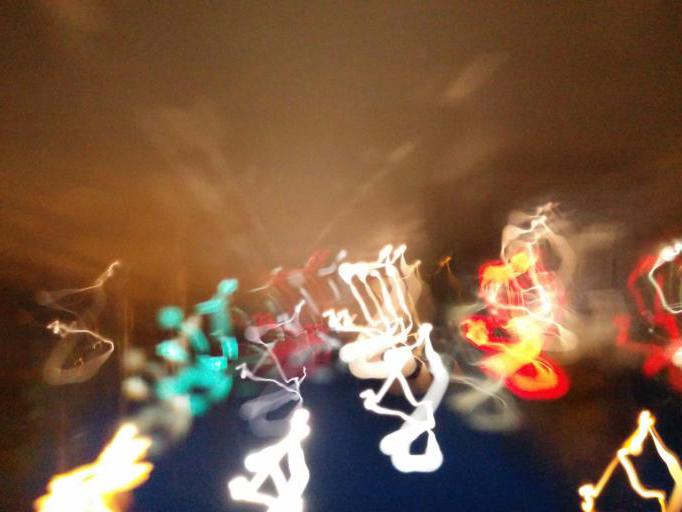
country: US
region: Washington
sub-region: King County
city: Seattle
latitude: 47.6686
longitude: -122.3663
